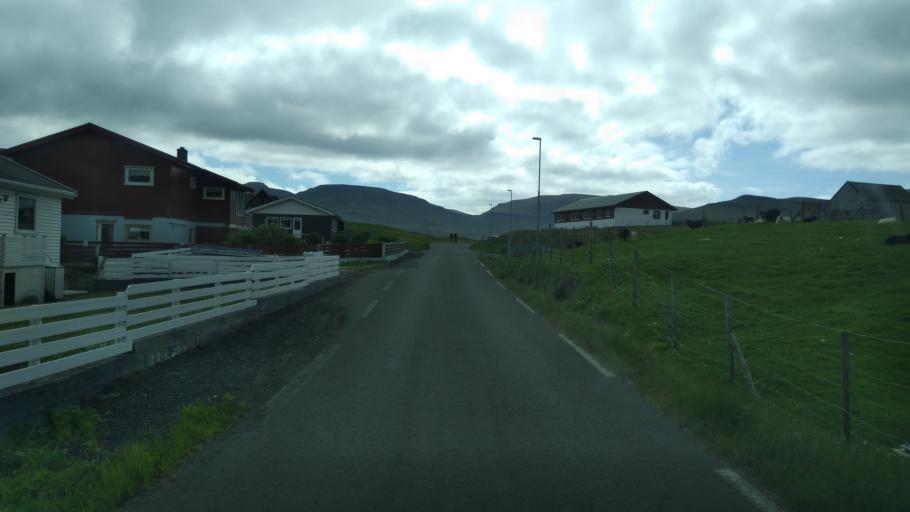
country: FO
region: Suduroy
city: Tvoroyri
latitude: 61.5465
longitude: -6.7792
